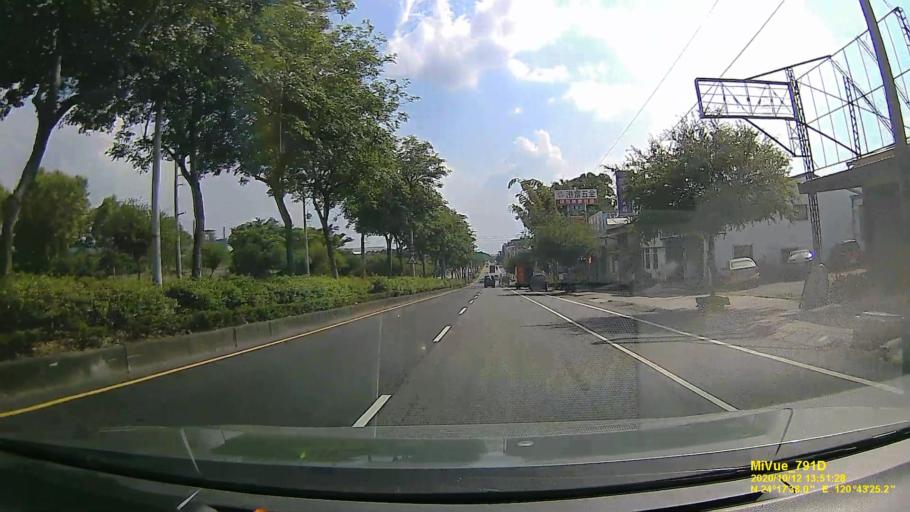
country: TW
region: Taiwan
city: Fengyuan
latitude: 24.2940
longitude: 120.7237
